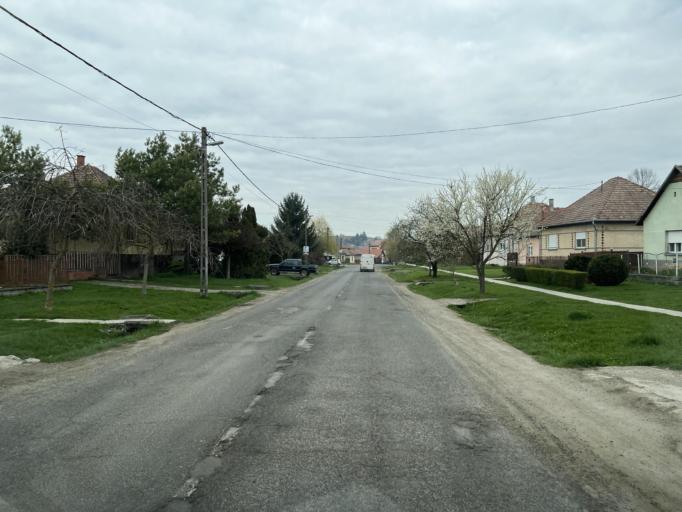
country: HU
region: Pest
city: Acsa
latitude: 47.7926
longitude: 19.3860
